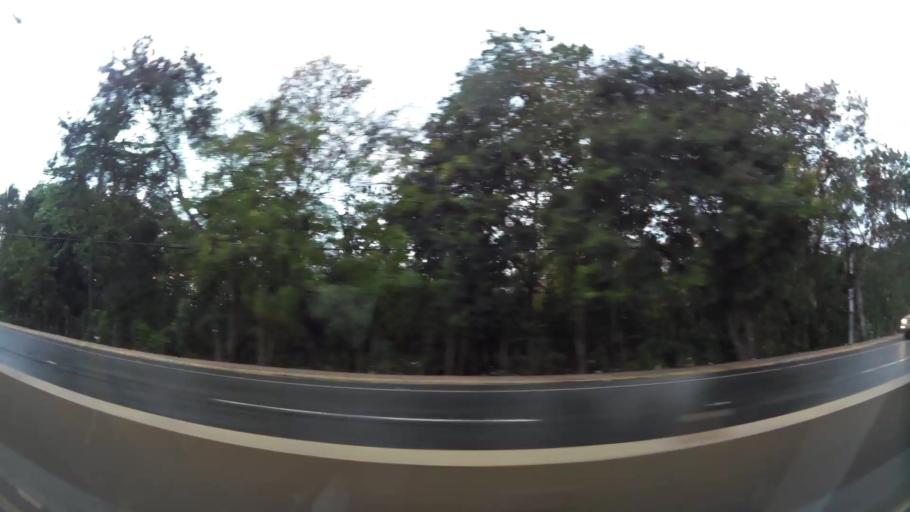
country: DO
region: Santo Domingo
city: Santo Domingo Oeste
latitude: 18.5698
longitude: -70.0944
